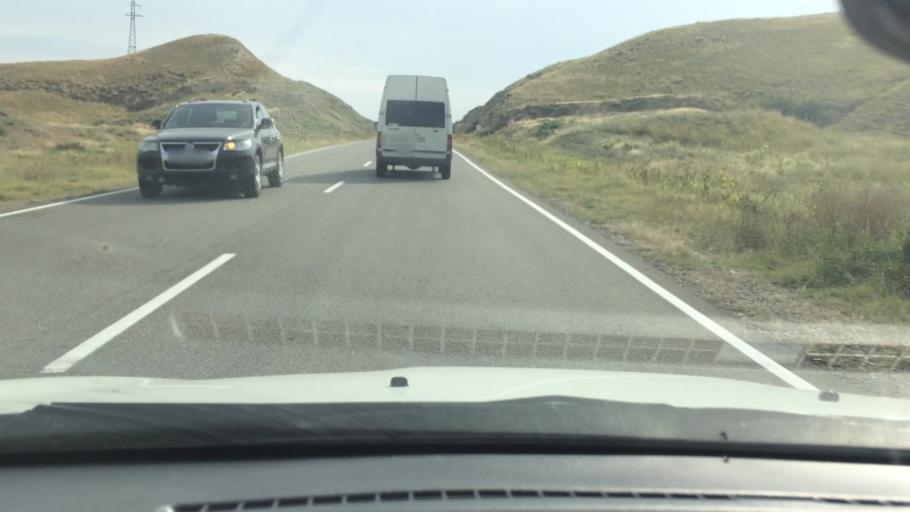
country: GE
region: Kvemo Kartli
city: Rust'avi
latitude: 41.5251
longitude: 44.9881
